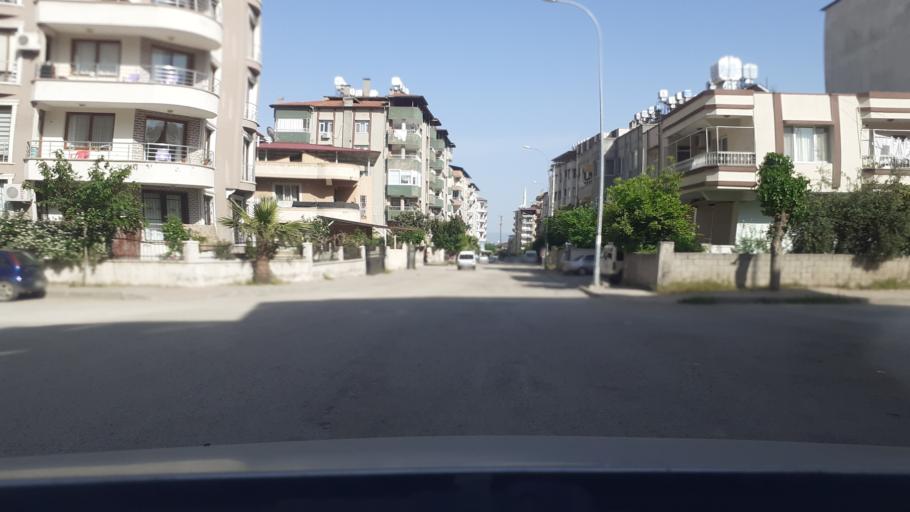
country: TR
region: Hatay
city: Kirikhan
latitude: 36.4964
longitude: 36.3650
